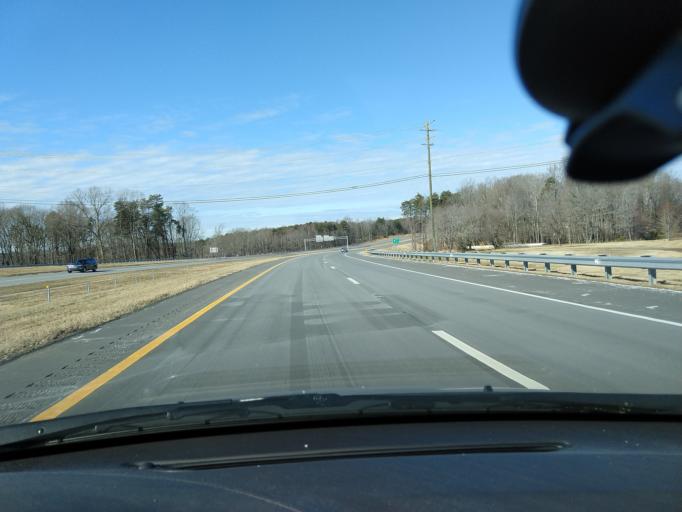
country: US
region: North Carolina
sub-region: Guilford County
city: Oak Ridge
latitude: 36.1252
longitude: -79.9631
